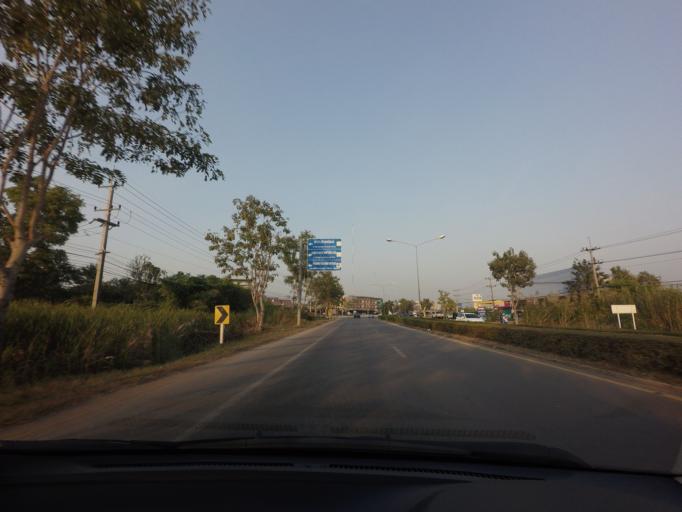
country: TH
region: Sukhothai
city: Sukhothai
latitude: 17.0211
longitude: 99.8137
